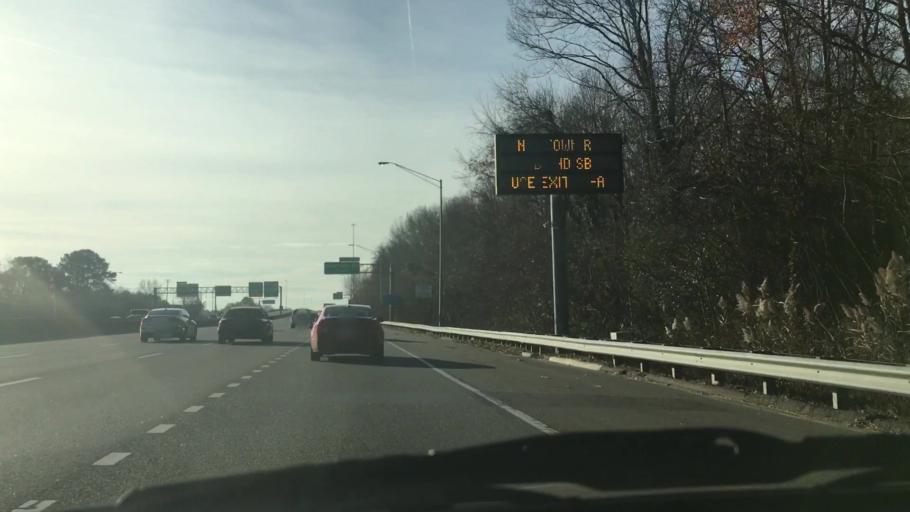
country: US
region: Virginia
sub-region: City of Chesapeake
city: Chesapeake
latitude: 36.8611
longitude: -76.1959
